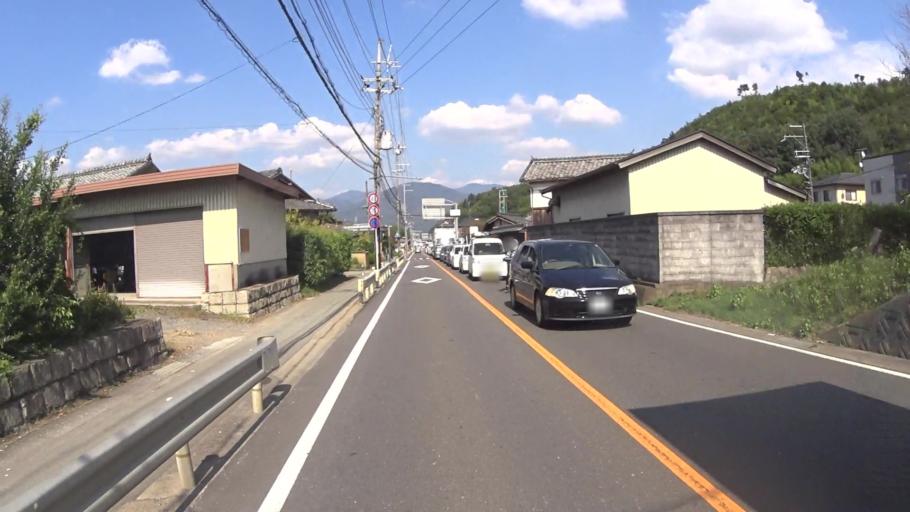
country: JP
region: Kyoto
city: Kameoka
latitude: 35.0092
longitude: 135.5616
